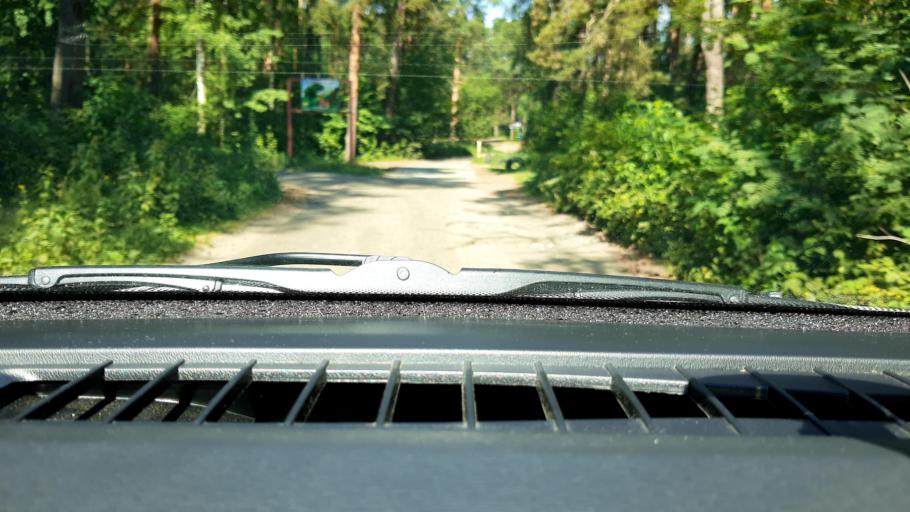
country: RU
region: Nizjnij Novgorod
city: Burevestnik
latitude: 56.1972
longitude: 43.7981
